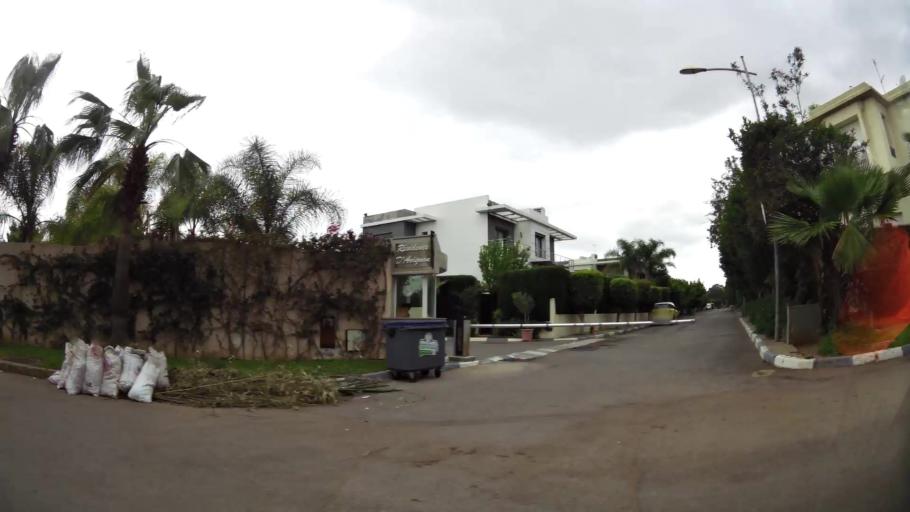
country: MA
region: Grand Casablanca
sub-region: Casablanca
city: Casablanca
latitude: 33.5249
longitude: -7.6333
